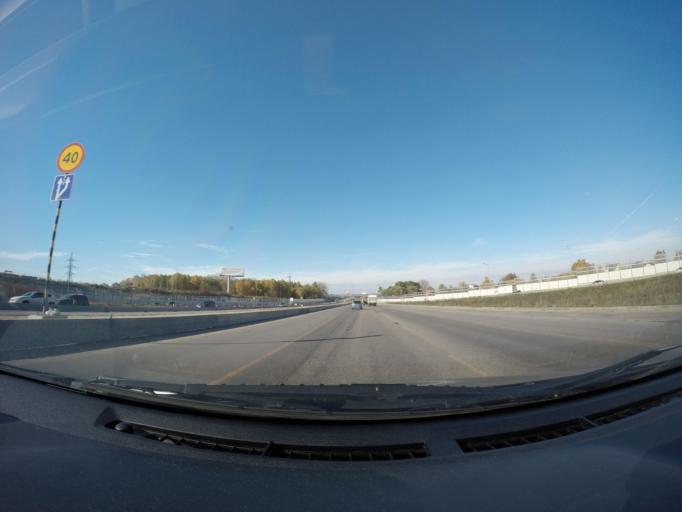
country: RU
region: Moskovskaya
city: Tomilino
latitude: 55.6302
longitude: 37.9419
